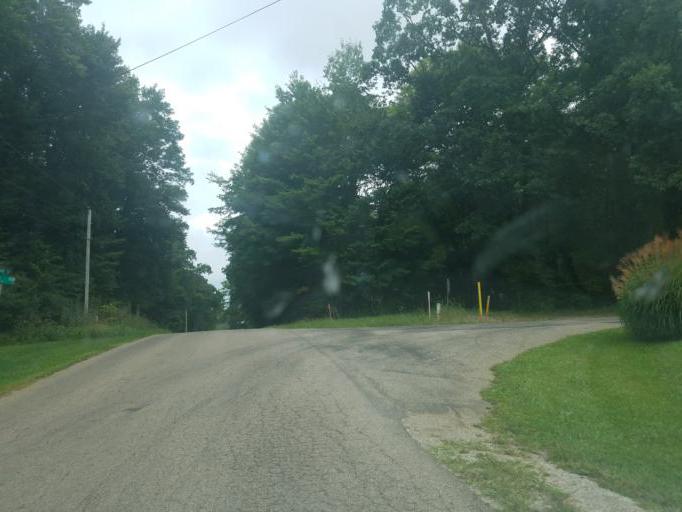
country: US
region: Ohio
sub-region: Knox County
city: Danville
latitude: 40.4558
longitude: -82.3271
